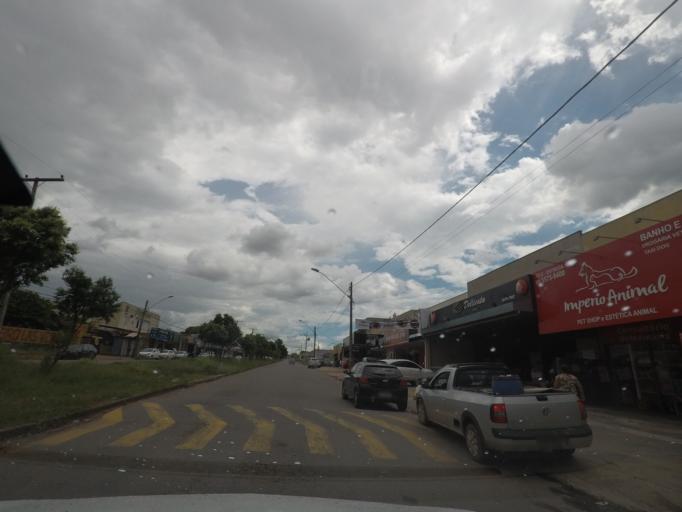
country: BR
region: Goias
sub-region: Goiania
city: Goiania
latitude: -16.7319
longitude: -49.3415
